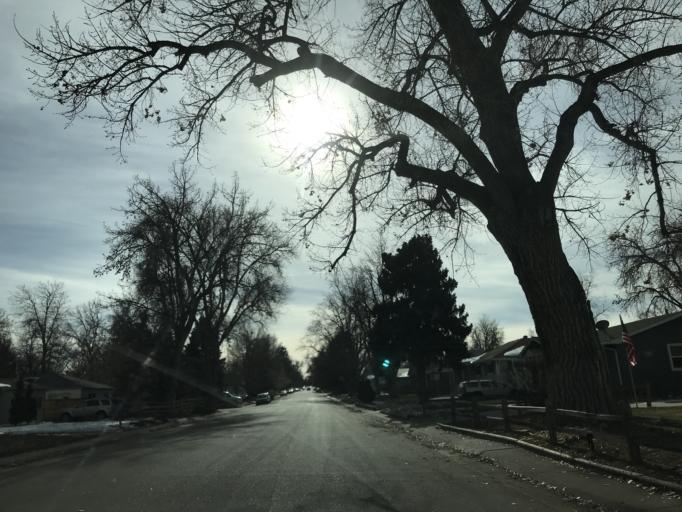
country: US
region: Colorado
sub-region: Arapahoe County
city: Littleton
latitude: 39.6058
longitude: -105.0116
